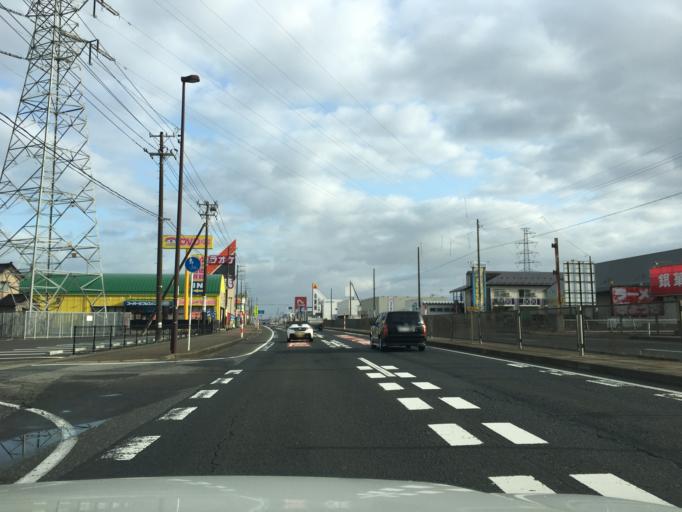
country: JP
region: Yamagata
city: Sakata
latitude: 38.8978
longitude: 139.8554
